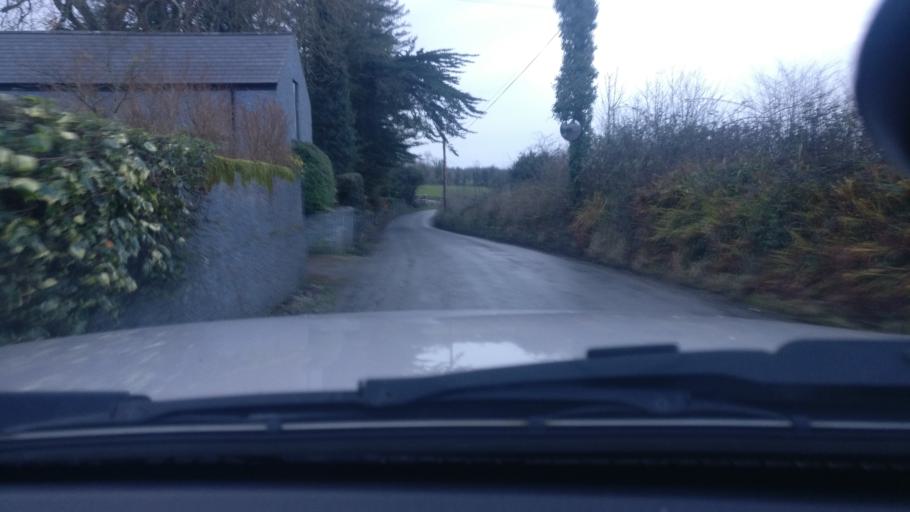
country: IE
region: Connaught
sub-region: County Galway
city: Loughrea
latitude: 53.1634
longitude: -8.5679
